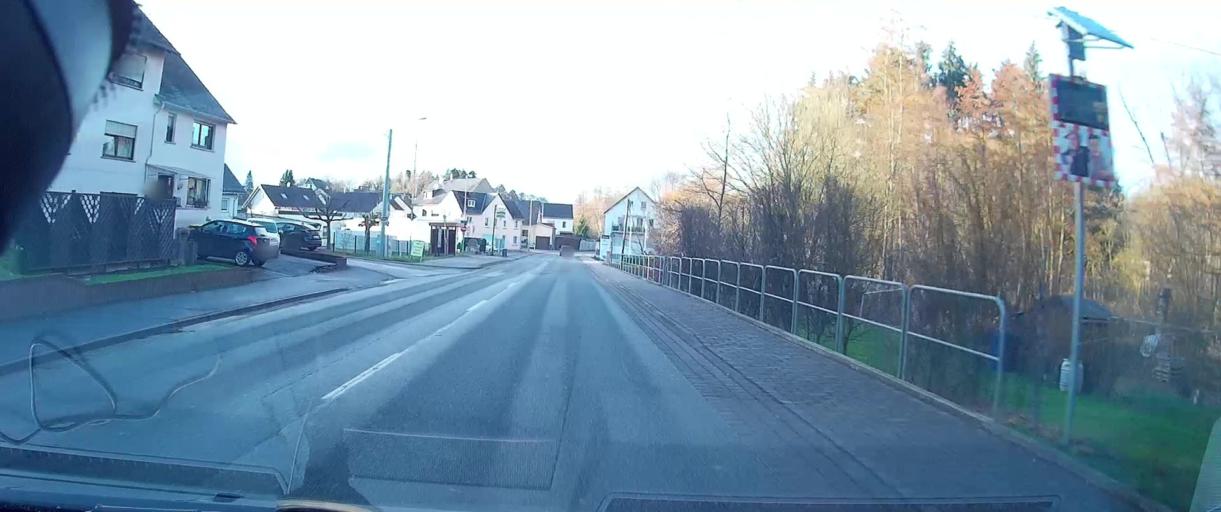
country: DE
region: Rheinland-Pfalz
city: Montabaur
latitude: 50.4461
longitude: 7.8163
